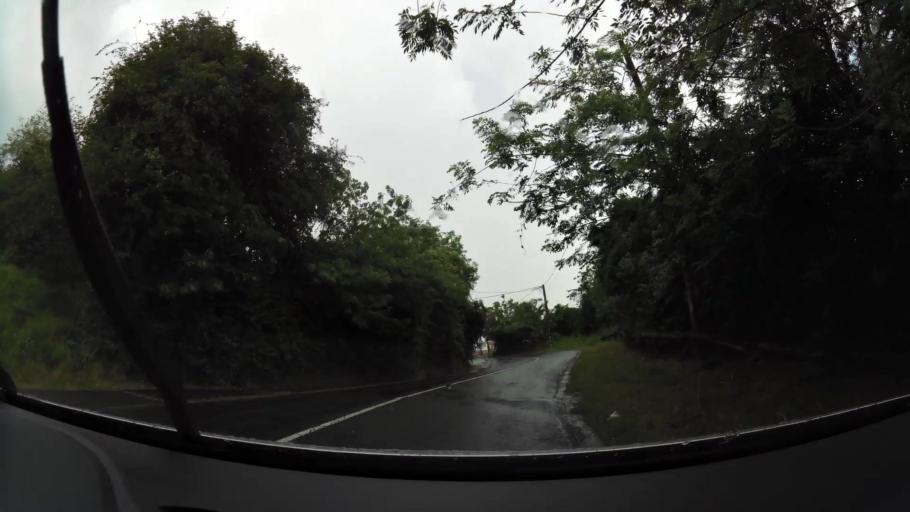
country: MQ
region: Martinique
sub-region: Martinique
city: Les Trois-Ilets
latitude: 14.5438
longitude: -61.0471
